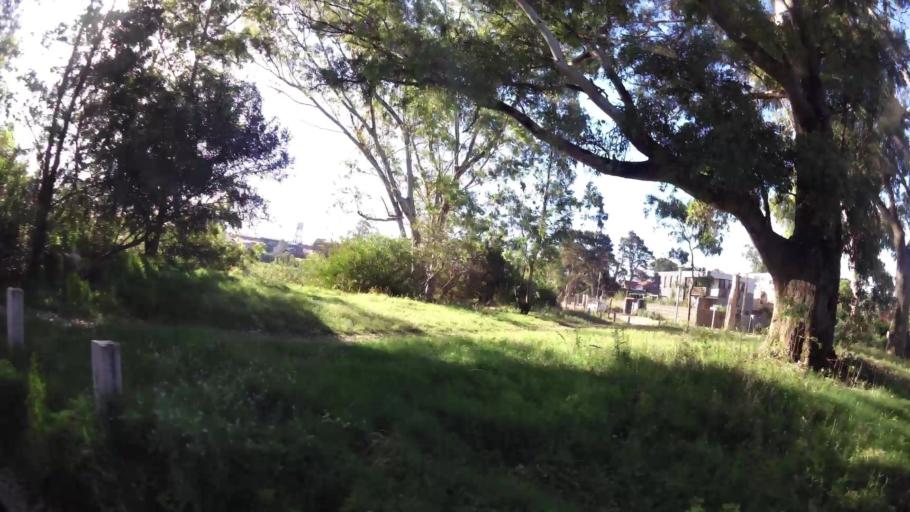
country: UY
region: Canelones
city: Paso de Carrasco
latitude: -34.8586
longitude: -56.0381
